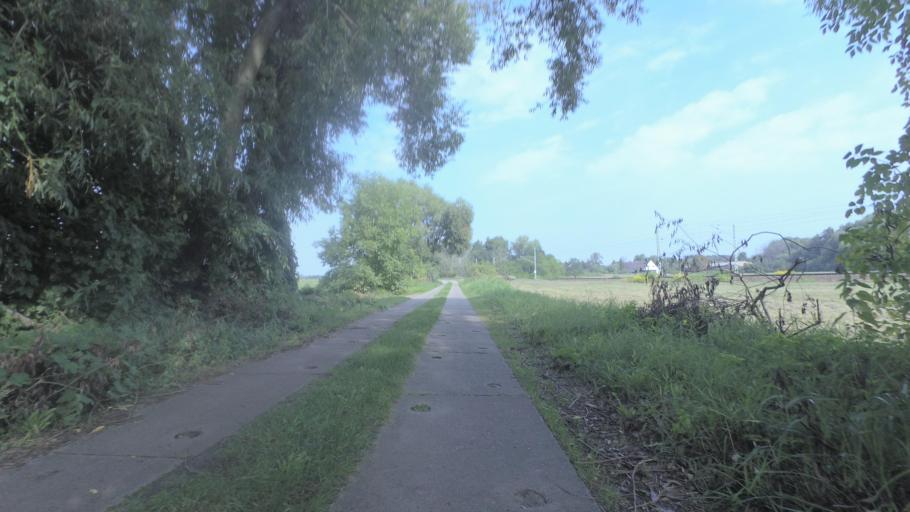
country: DE
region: Brandenburg
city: Rangsdorf
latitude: 52.2710
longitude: 13.4358
